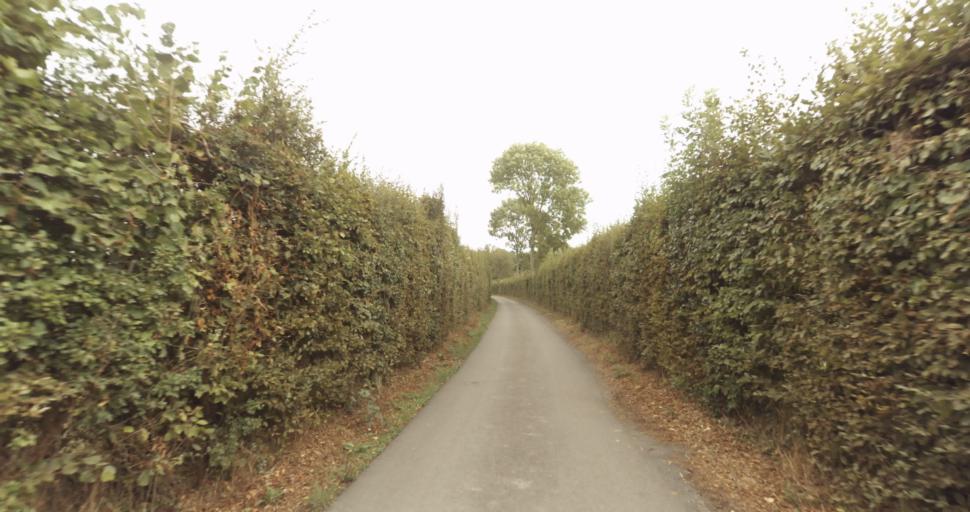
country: FR
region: Lower Normandy
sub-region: Departement de l'Orne
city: Gace
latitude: 48.8707
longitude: 0.3053
